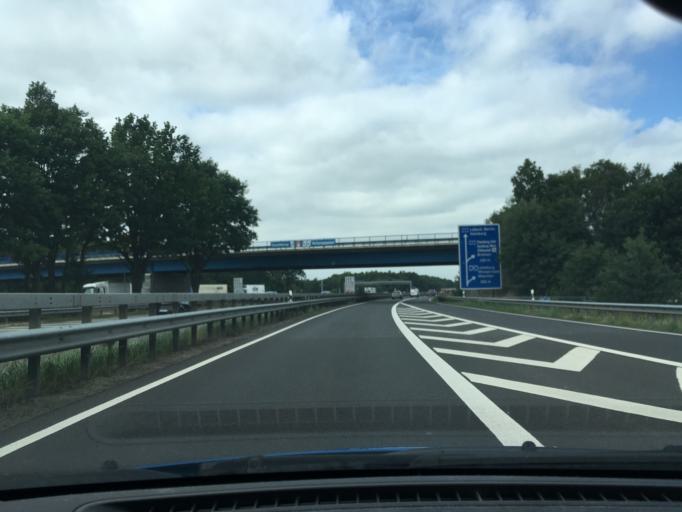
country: DE
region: Lower Saxony
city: Harmstorf
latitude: 53.3853
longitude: 10.0210
